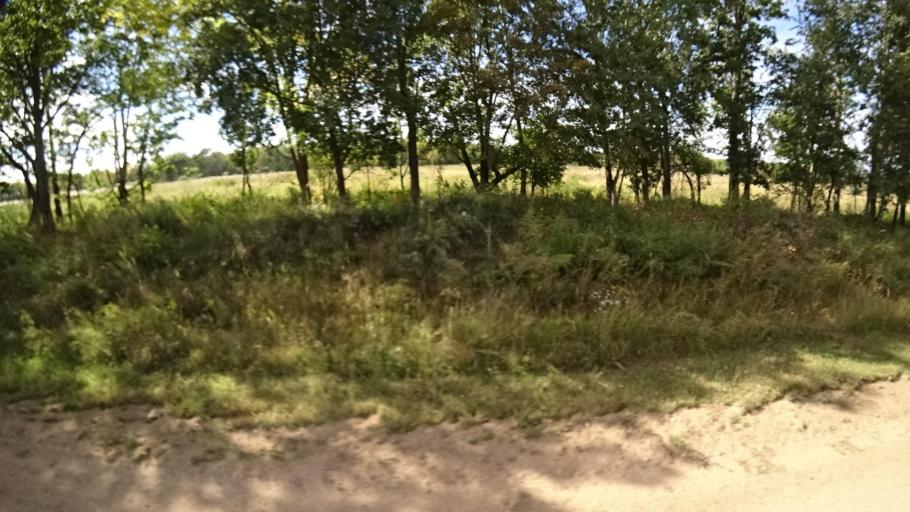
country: RU
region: Primorskiy
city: Yakovlevka
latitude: 44.4214
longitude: 133.5717
